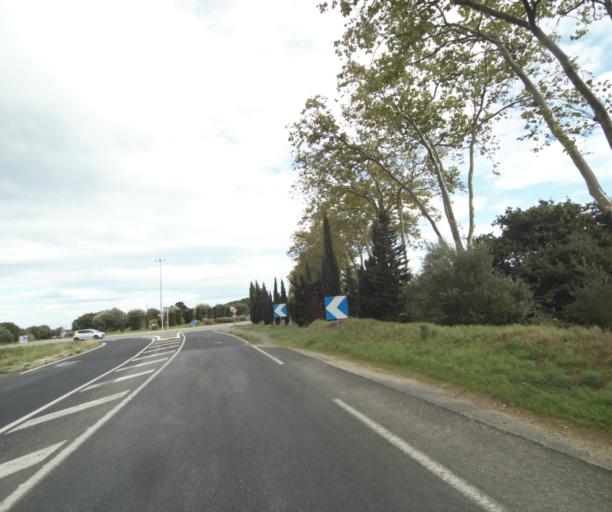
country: FR
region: Languedoc-Roussillon
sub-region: Departement des Pyrenees-Orientales
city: Sant Andreu de Sureda
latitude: 42.5510
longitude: 2.9964
